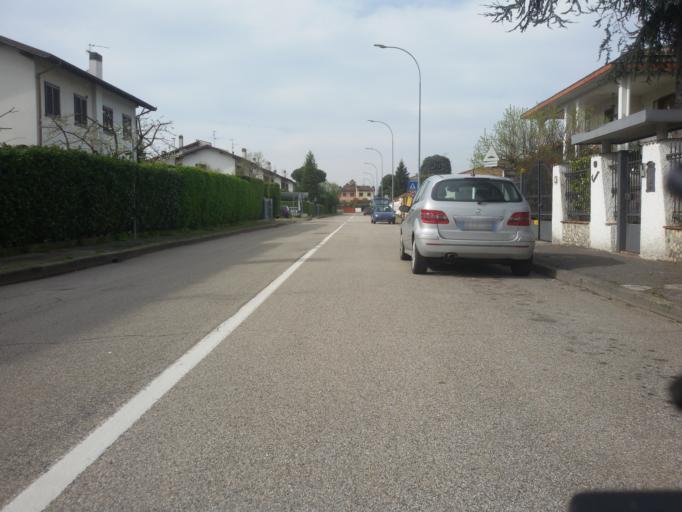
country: IT
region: Lombardy
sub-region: Citta metropolitana di Milano
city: Noviglio
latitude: 45.3596
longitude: 9.0500
